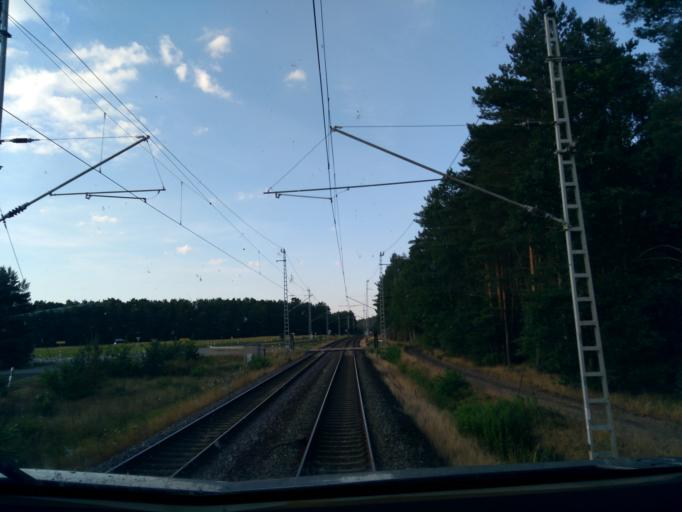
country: DE
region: Mecklenburg-Vorpommern
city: Ludwigslust
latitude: 53.3595
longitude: 11.4706
